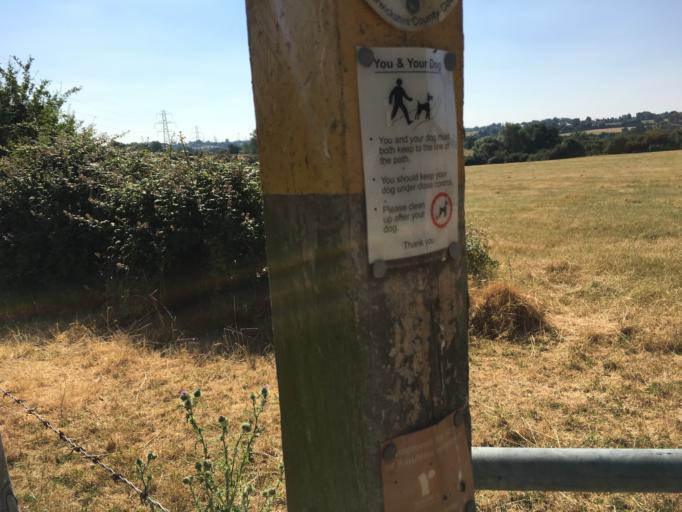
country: GB
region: England
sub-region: Warwickshire
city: Rugby
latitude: 52.3967
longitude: -1.2292
